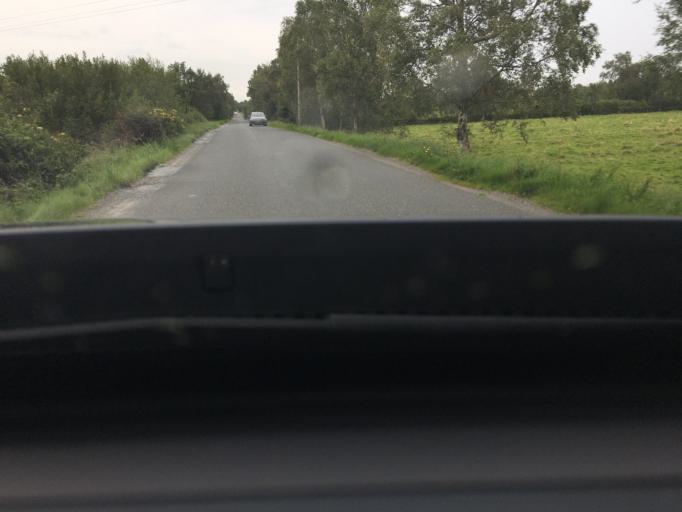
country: GB
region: Northern Ireland
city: Moy
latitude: 54.5099
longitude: -6.6355
